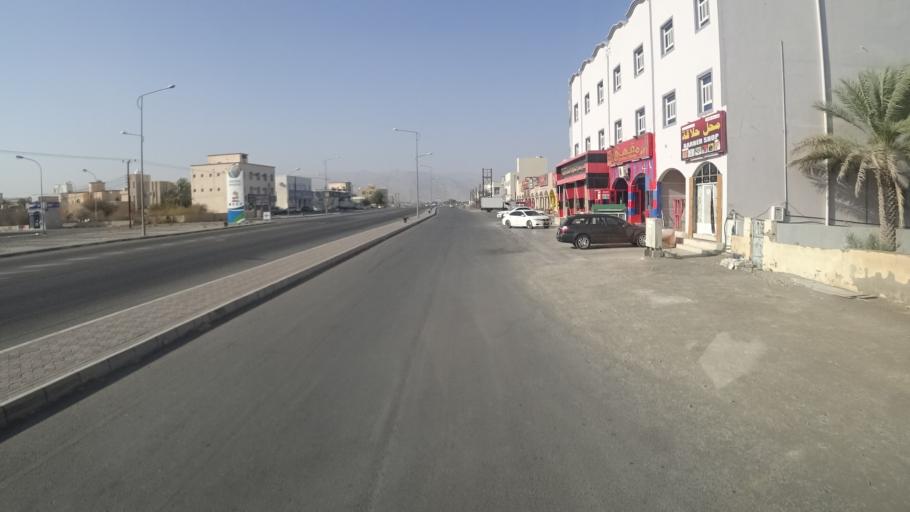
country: OM
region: Muhafazat ad Dakhiliyah
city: Izki
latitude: 22.8269
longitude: 57.7549
